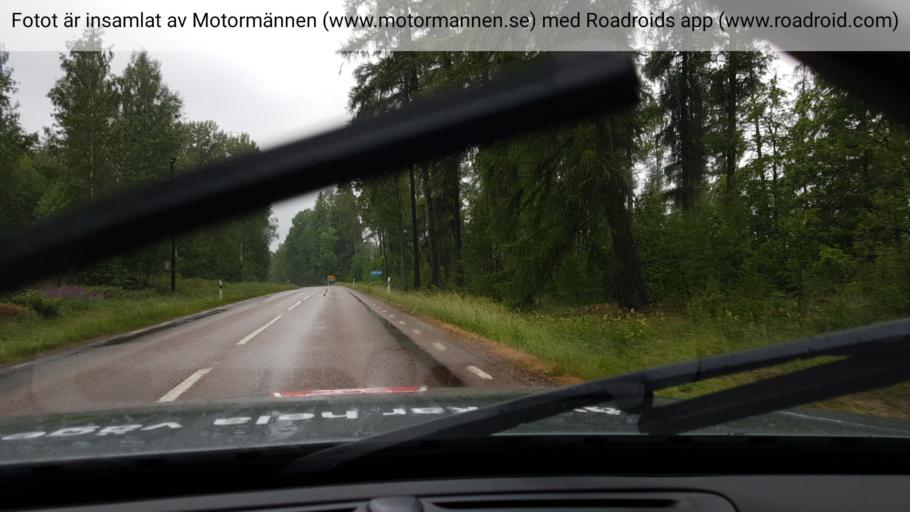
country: SE
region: Vaestmanland
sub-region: Norbergs Kommun
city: Norberg
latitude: 60.0223
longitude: 16.0223
